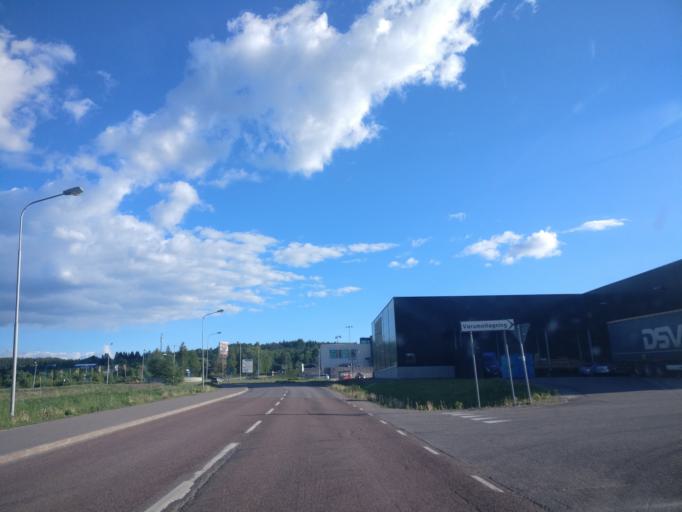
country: SE
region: Vaesternorrland
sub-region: Sundsvalls Kommun
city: Sundsbruk
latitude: 62.4450
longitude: 17.3416
